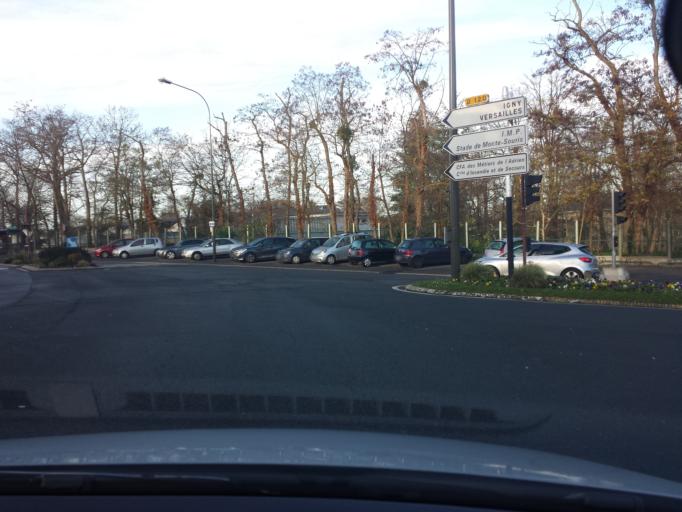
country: FR
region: Ile-de-France
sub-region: Departement de l'Essonne
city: Palaiseau
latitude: 48.7314
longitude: 2.2548
